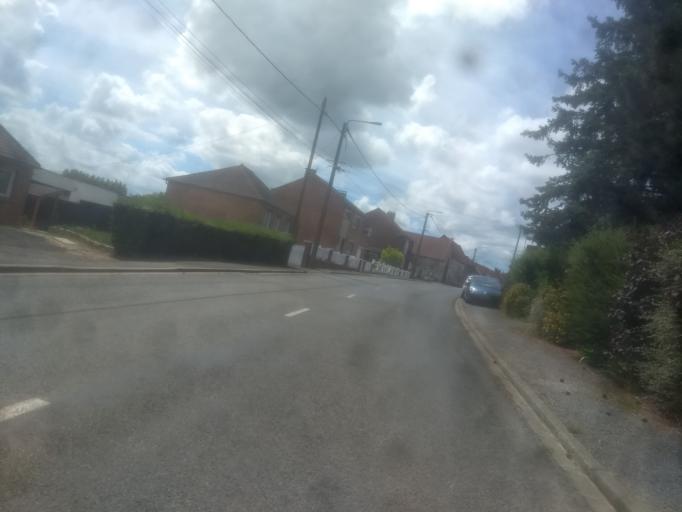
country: FR
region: Nord-Pas-de-Calais
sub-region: Departement du Pas-de-Calais
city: Mont-Saint-Eloi
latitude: 50.3463
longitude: 2.6626
